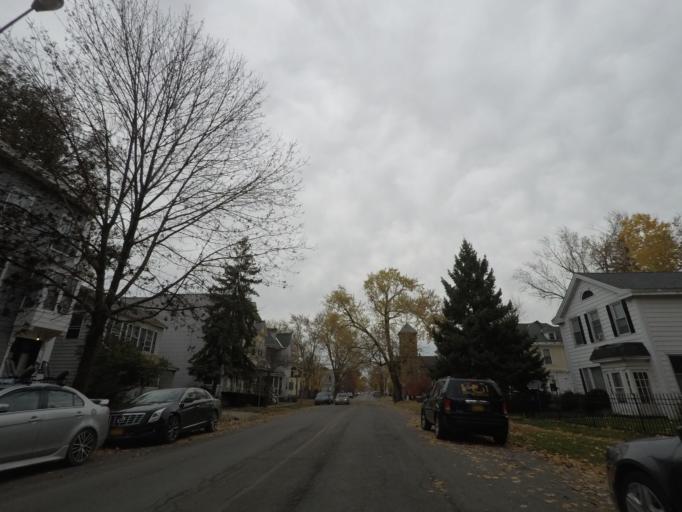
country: US
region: New York
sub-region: Saratoga County
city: Waterford
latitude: 42.7738
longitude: -73.6764
